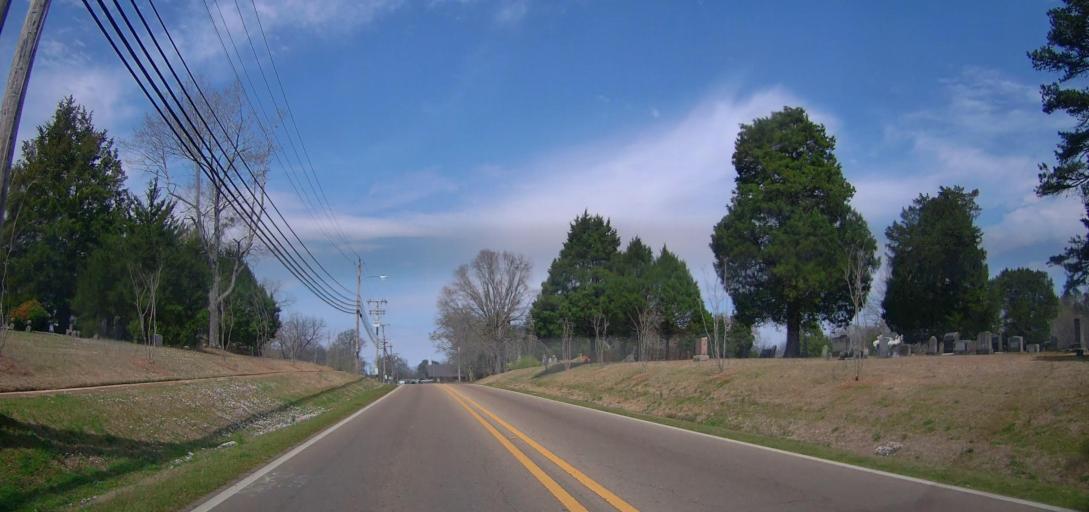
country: US
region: Mississippi
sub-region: Union County
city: New Albany
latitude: 34.4840
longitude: -89.0008
